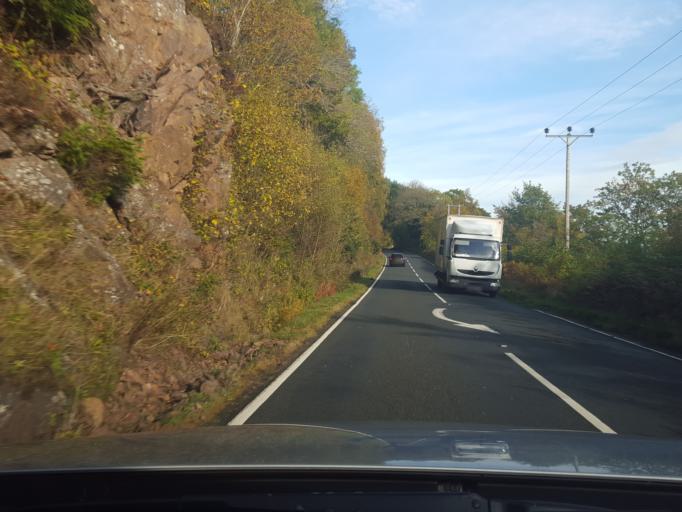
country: GB
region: Scotland
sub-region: Highland
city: Beauly
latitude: 57.2597
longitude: -4.5232
